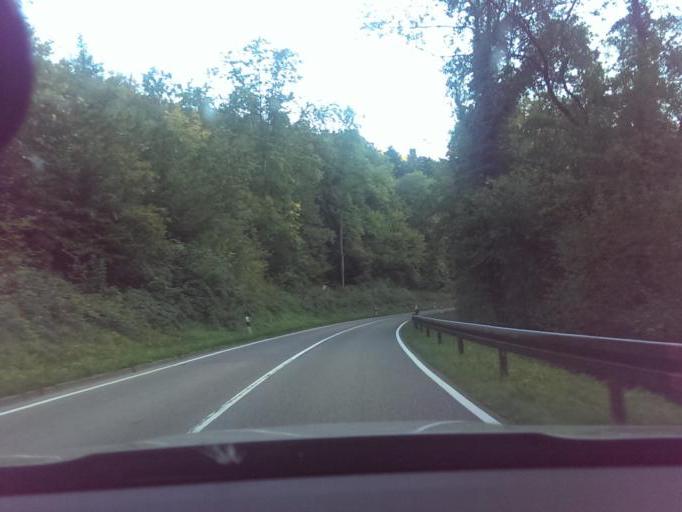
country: DE
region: Baden-Wuerttemberg
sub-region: Karlsruhe Region
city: Unterreichenbach
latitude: 48.8422
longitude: 8.7494
